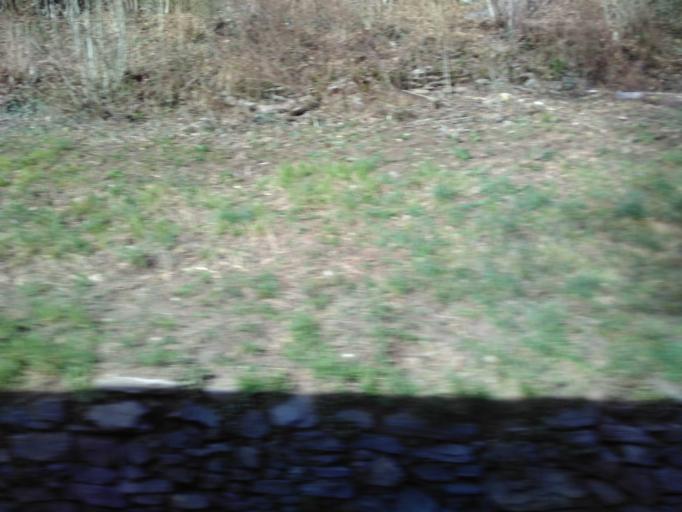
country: CH
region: Ticino
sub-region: Locarno District
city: Verscio
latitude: 46.2321
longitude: 8.7332
